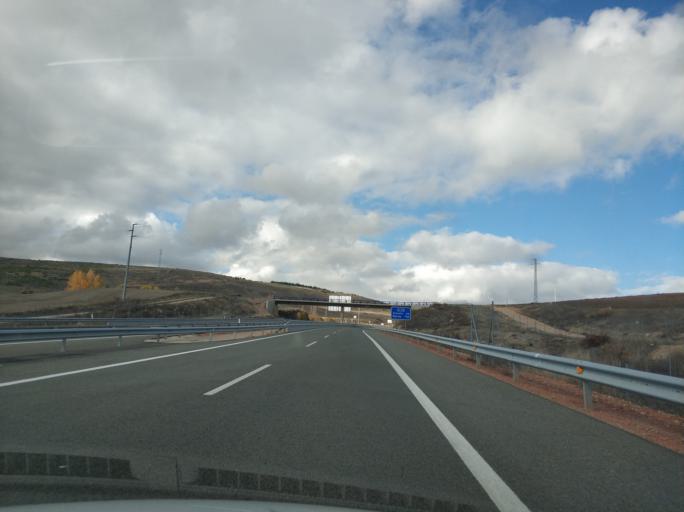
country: ES
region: Castille and Leon
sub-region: Provincia de Soria
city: Medinaceli
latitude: 41.1820
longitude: -2.4290
